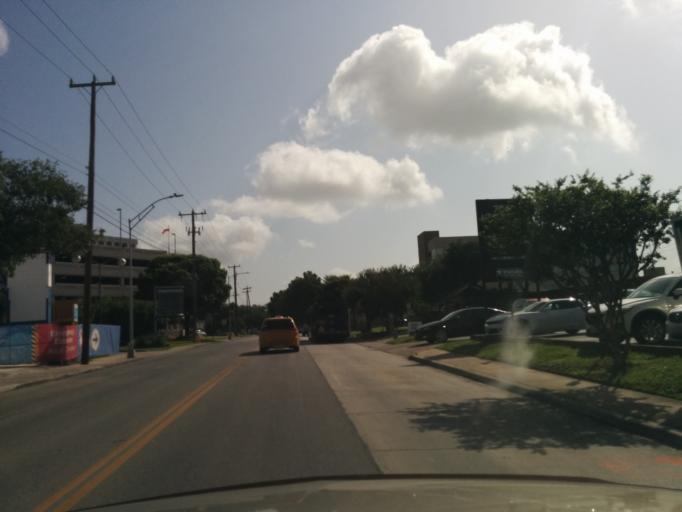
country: US
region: Texas
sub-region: Bexar County
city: Balcones Heights
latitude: 29.5065
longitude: -98.5715
